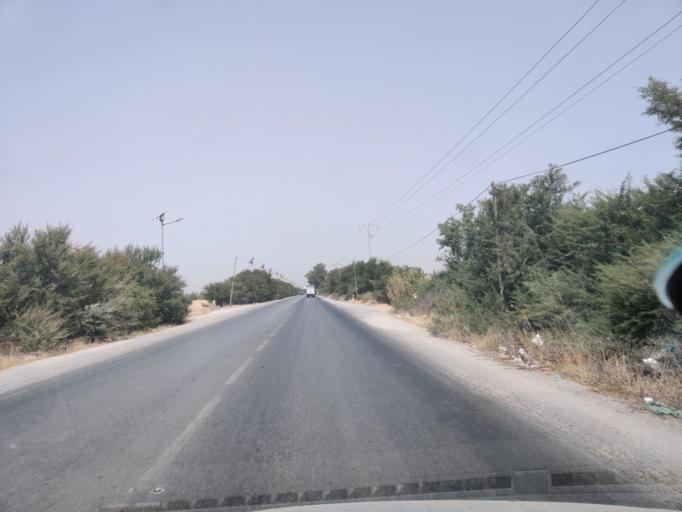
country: TN
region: Tunis
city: La Sebala du Mornag
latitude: 36.6542
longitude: 10.3338
